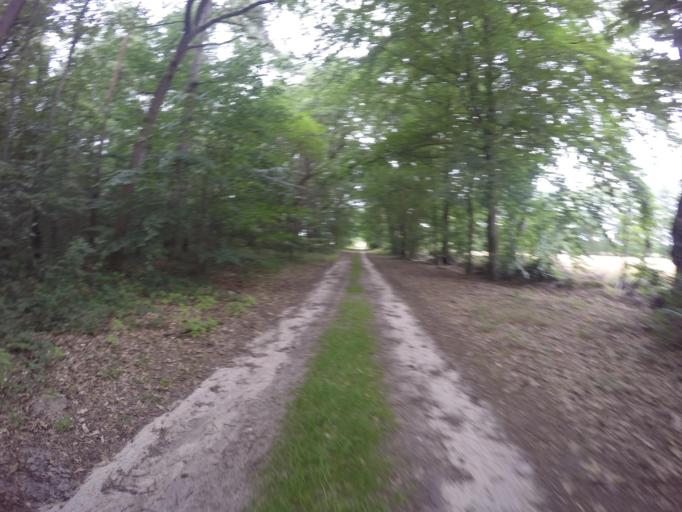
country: DE
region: Lower Saxony
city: Thomasburg
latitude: 53.2591
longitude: 10.6973
